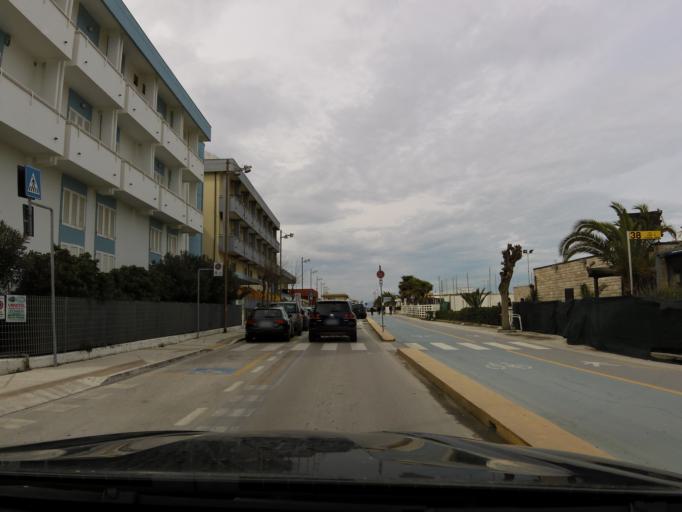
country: IT
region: The Marches
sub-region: Provincia di Macerata
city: Civitanova Marche
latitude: 43.3274
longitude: 13.7154
